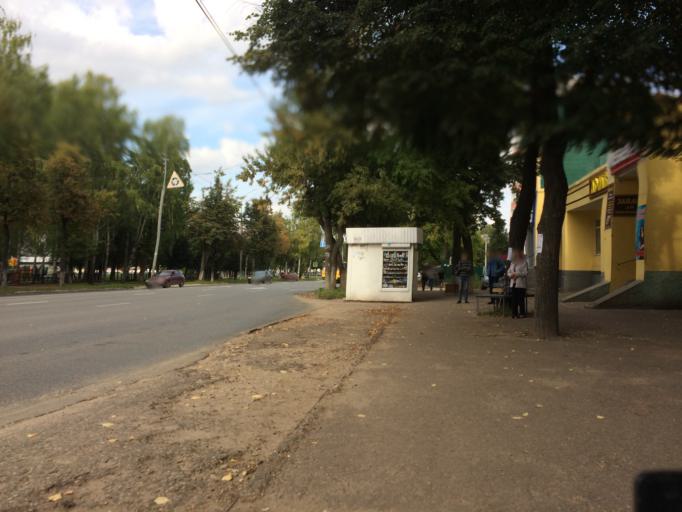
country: RU
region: Mariy-El
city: Yoshkar-Ola
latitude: 56.6381
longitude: 47.8682
